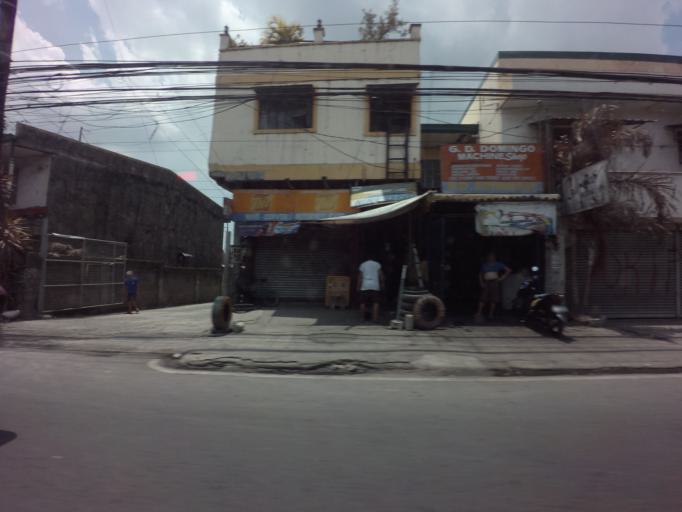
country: PH
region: Calabarzon
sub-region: Province of Laguna
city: San Pedro
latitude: 14.4037
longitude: 121.0471
